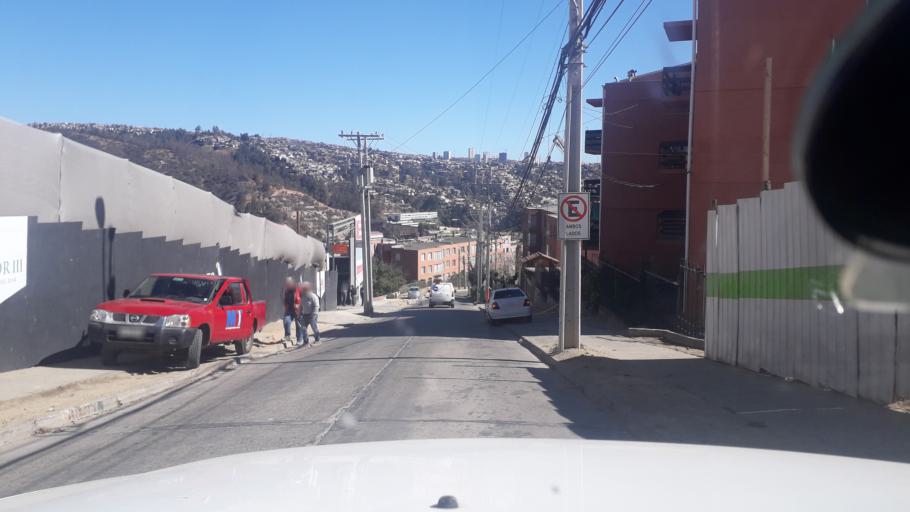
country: CL
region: Valparaiso
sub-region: Provincia de Valparaiso
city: Vina del Mar
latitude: -33.0376
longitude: -71.5141
